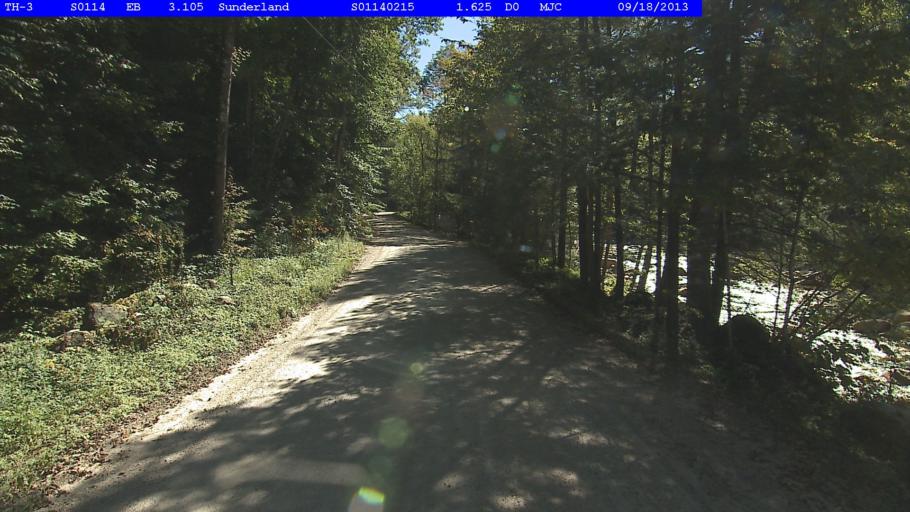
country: US
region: Vermont
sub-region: Bennington County
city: Arlington
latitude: 43.0501
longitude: -73.1158
